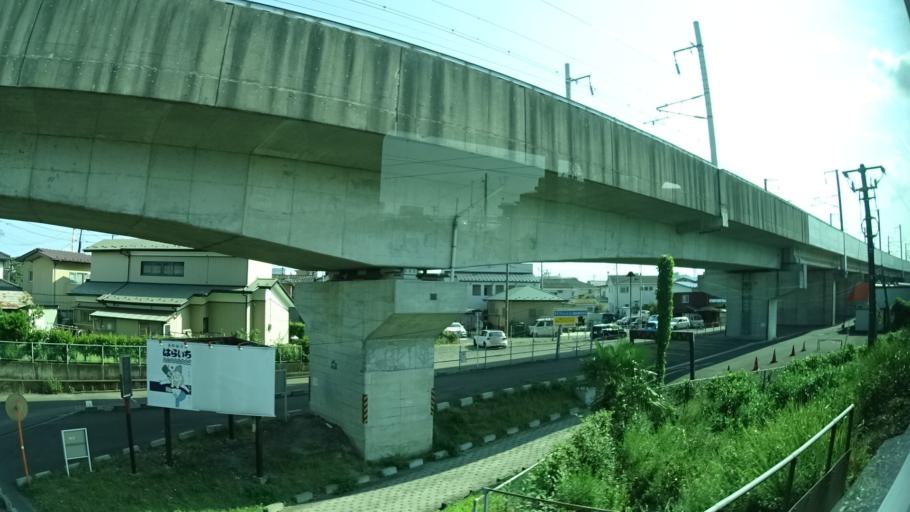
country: JP
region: Miyagi
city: Sendai-shi
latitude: 38.2709
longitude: 140.9098
